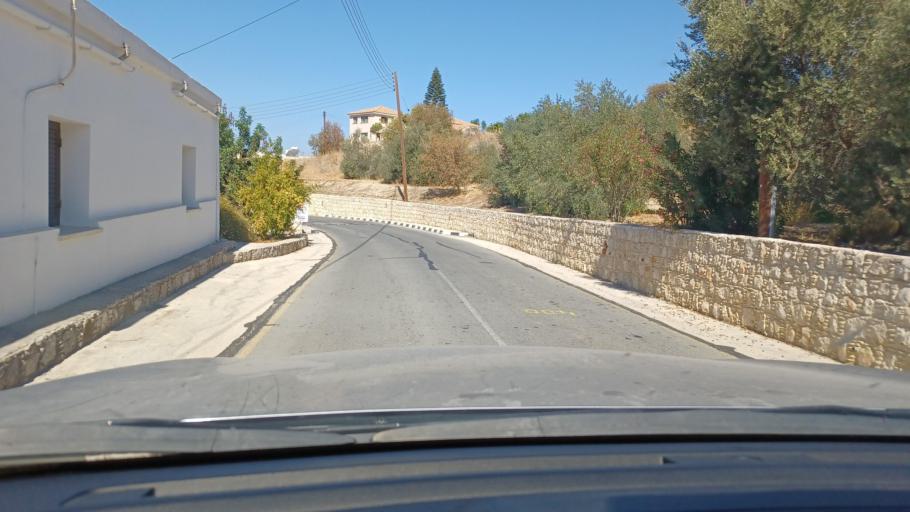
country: CY
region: Pafos
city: Polis
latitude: 34.9992
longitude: 32.4713
